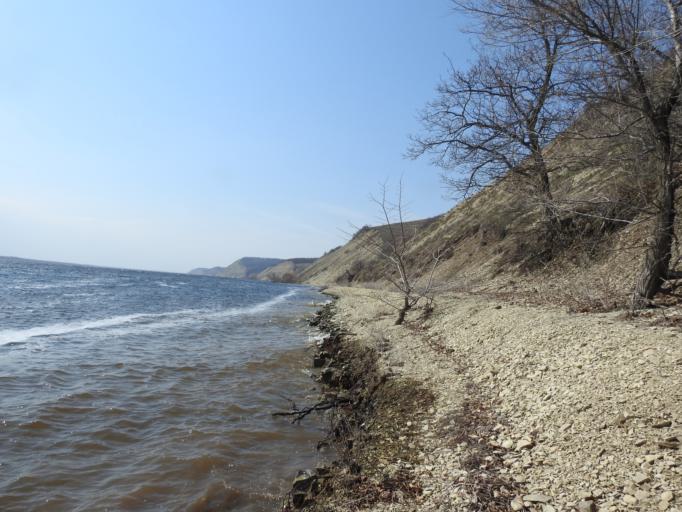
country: RU
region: Saratov
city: Voskresenskoye
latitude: 51.7936
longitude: 46.8628
